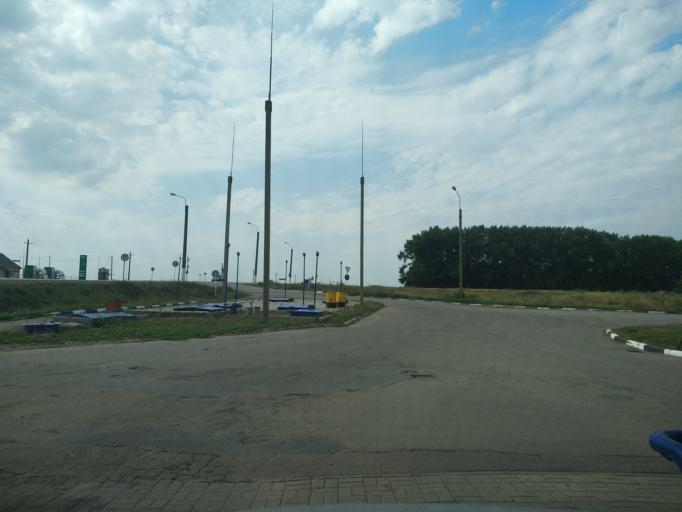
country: RU
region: Lipetsk
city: Dobrinka
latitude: 51.9021
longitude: 40.4548
